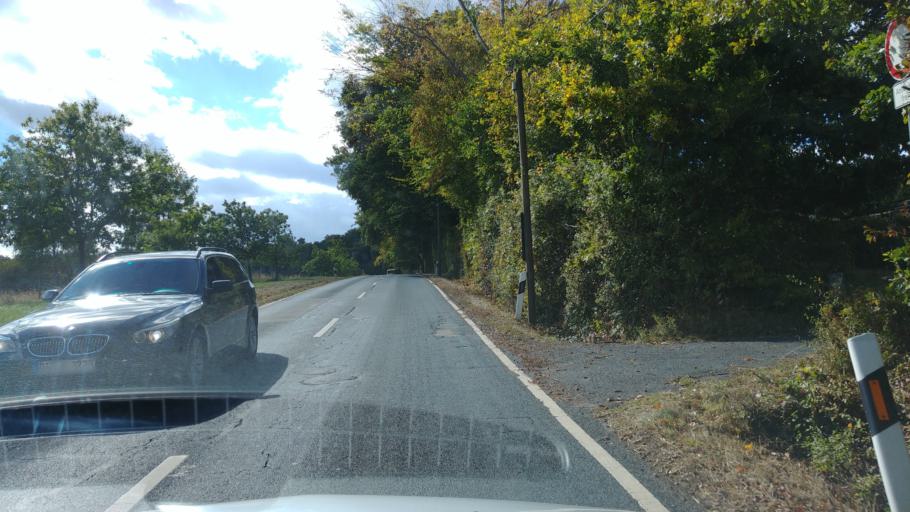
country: DE
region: Hesse
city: Taunusstein
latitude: 50.1004
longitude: 8.1888
